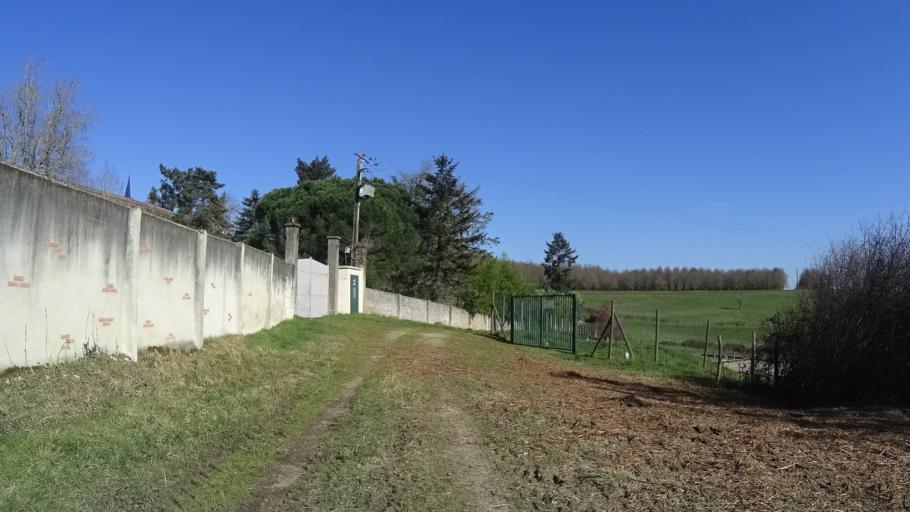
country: FR
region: Aquitaine
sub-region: Departement de la Dordogne
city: Saint-Aulaye
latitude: 45.1268
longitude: 0.2142
